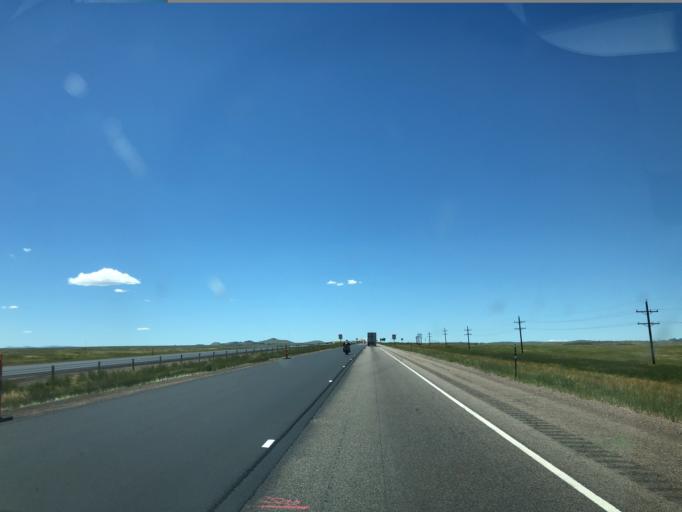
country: US
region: Wyoming
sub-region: Laramie County
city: Cheyenne
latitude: 41.1001
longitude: -105.0832
